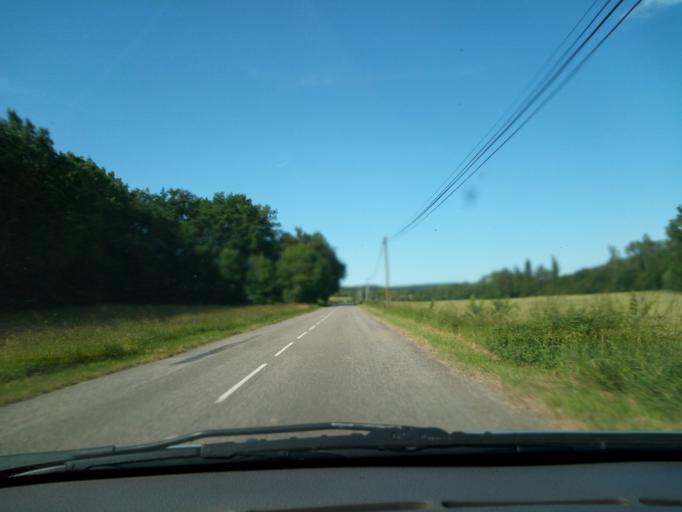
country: FR
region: Midi-Pyrenees
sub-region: Departement du Lot
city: Castelnau-Montratier
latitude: 44.2451
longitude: 1.3458
